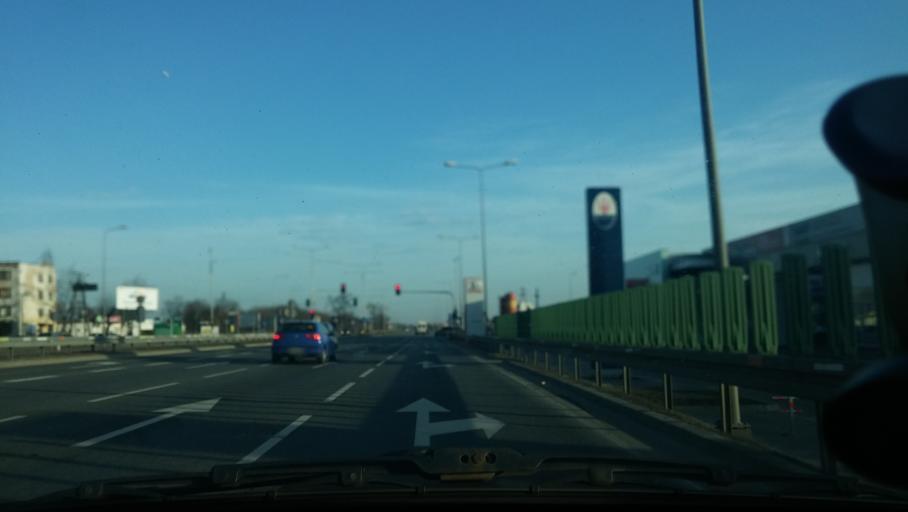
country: PL
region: Masovian Voivodeship
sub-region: Powiat piaseczynski
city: Mysiadlo
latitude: 52.0968
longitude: 21.0191
